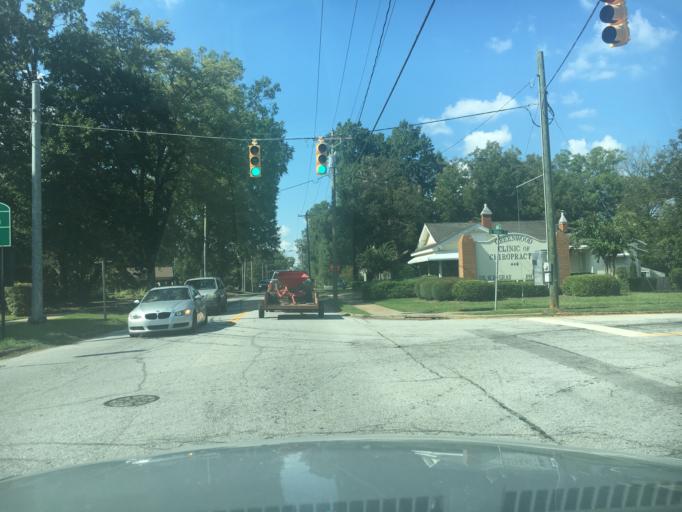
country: US
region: South Carolina
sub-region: Greenwood County
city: Greenwood
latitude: 34.2012
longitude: -82.1608
